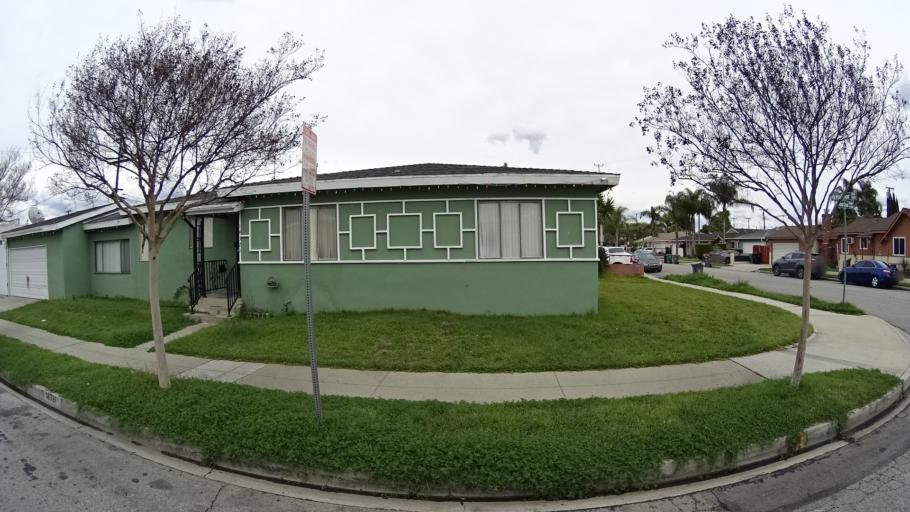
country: US
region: California
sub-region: Los Angeles County
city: West Puente Valley
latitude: 34.0670
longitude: -117.9641
